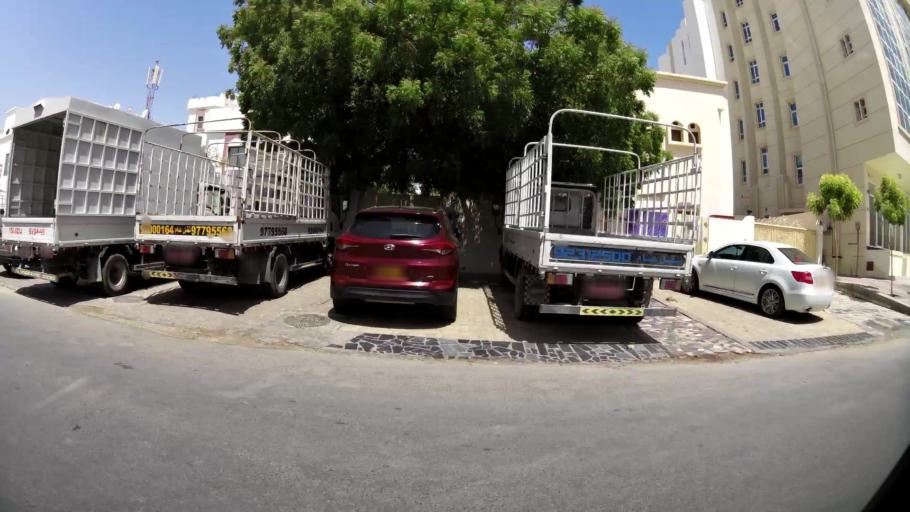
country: OM
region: Muhafazat Masqat
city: Bawshar
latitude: 23.5910
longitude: 58.4006
